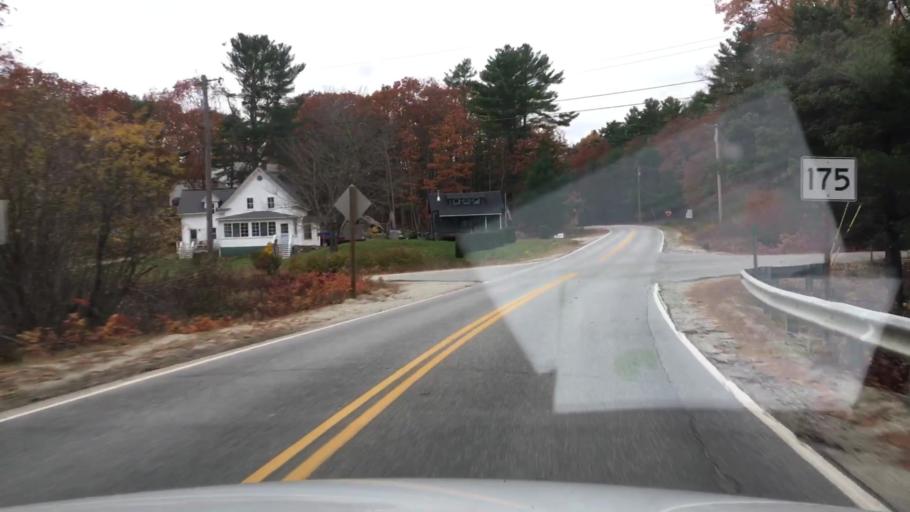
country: US
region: Maine
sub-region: Hancock County
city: Sedgwick
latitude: 44.3789
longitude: -68.5659
